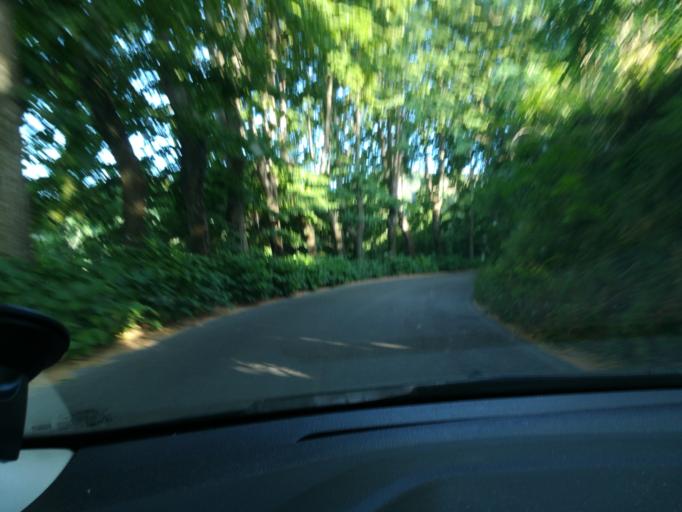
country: IT
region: Tuscany
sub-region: Provincia di Lucca
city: Stiava
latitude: 43.9164
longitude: 10.3400
